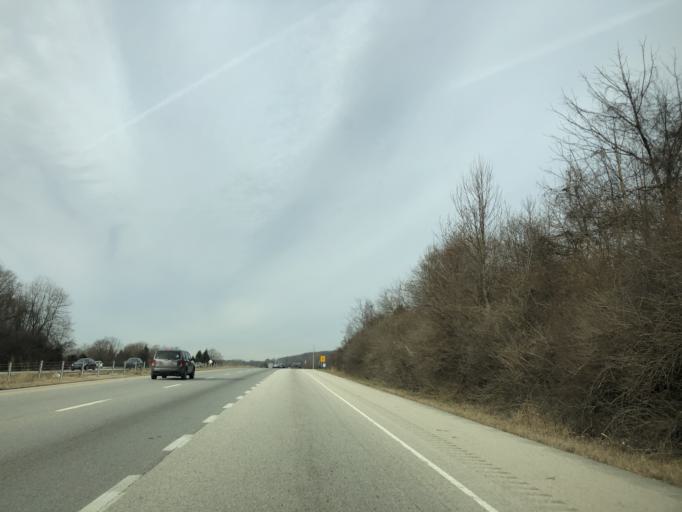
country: US
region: Pennsylvania
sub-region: Chester County
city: Downingtown
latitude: 40.0172
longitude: -75.6654
